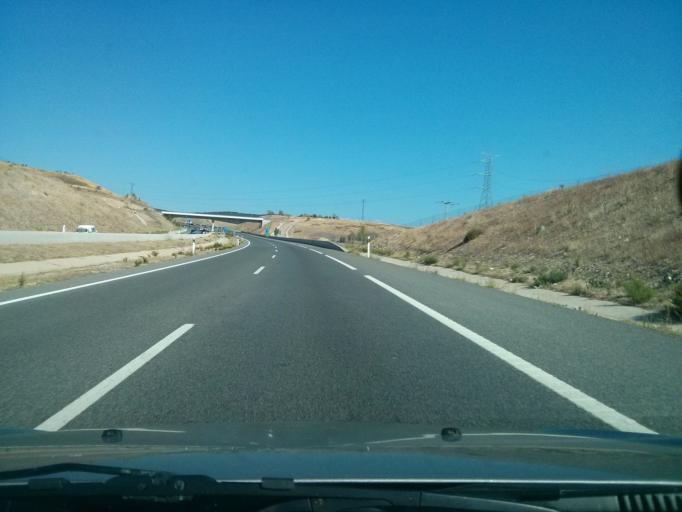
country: ES
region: Madrid
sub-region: Provincia de Madrid
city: El Molar
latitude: 40.7358
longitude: -3.5675
